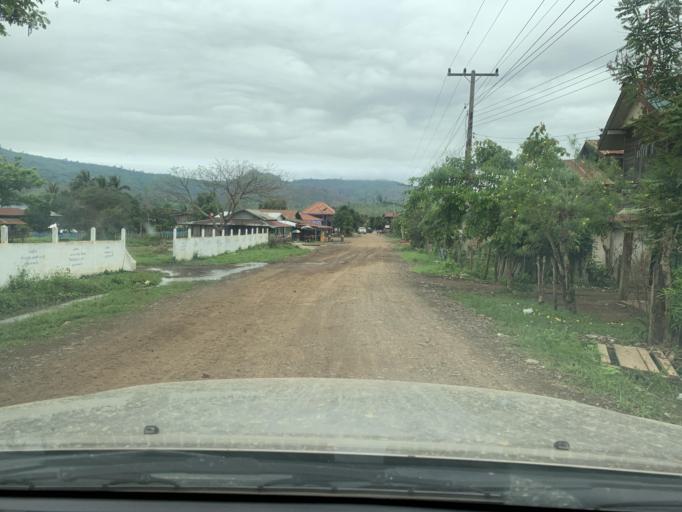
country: TH
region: Nan
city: Mae Charim
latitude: 18.4195
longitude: 101.4510
